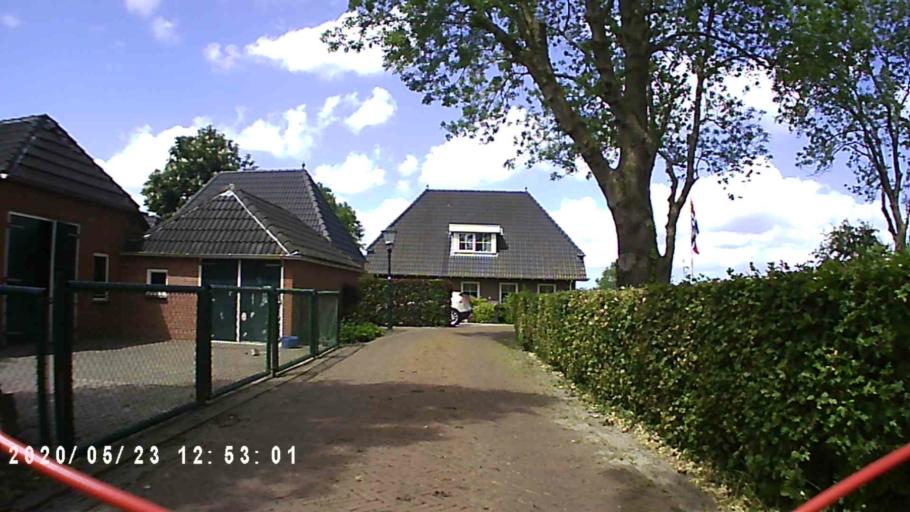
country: NL
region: Groningen
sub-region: Gemeente Delfzijl
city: Delfzijl
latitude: 53.2978
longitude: 7.0464
